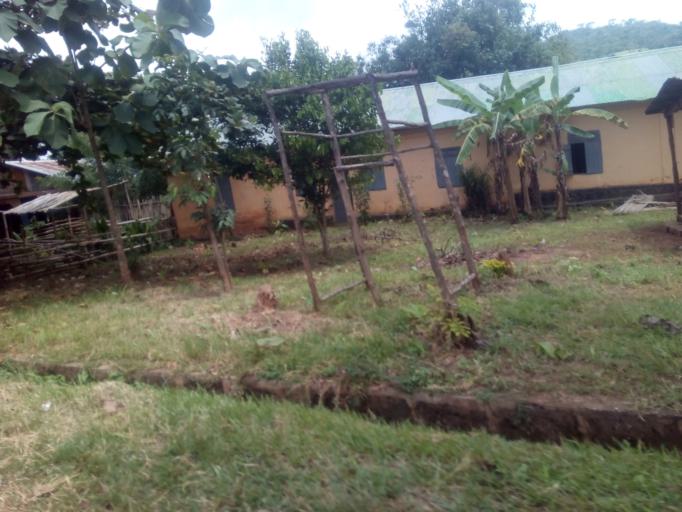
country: TG
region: Plateaux
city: Kpalime
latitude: 6.9425
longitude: 0.5991
